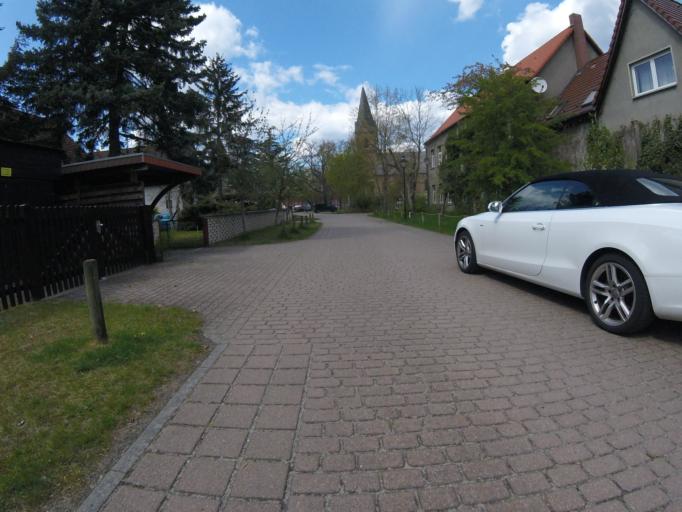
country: DE
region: Brandenburg
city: Munchehofe
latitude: 52.2220
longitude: 13.7668
